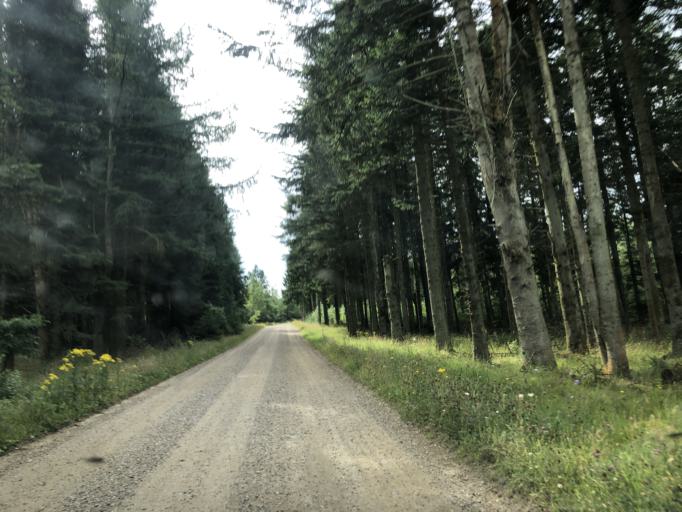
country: DK
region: Central Jutland
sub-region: Holstebro Kommune
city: Ulfborg
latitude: 56.2863
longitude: 8.4675
